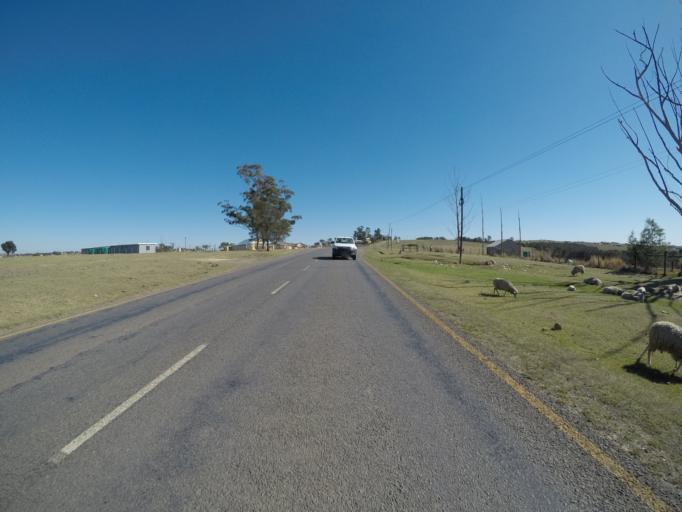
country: ZA
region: Eastern Cape
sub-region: OR Tambo District Municipality
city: Mthatha
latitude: -31.7978
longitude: 28.7453
